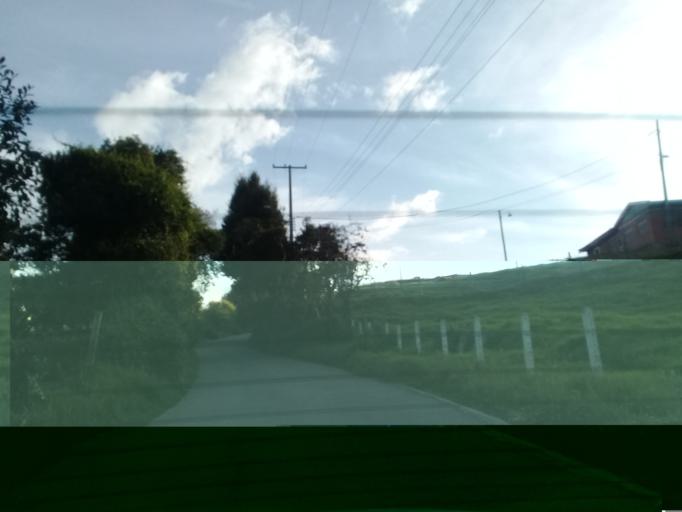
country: CO
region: Cundinamarca
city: Sibate
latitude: 4.4584
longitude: -74.2679
